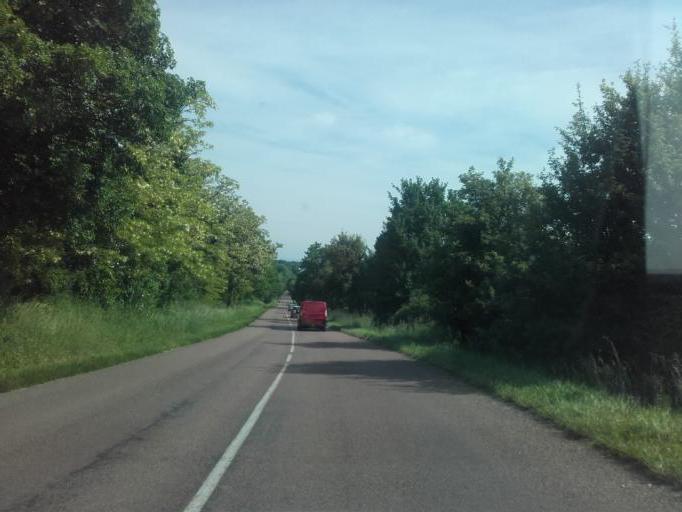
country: FR
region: Bourgogne
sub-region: Departement de Saone-et-Loire
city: Dracy-le-Fort
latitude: 46.7983
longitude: 4.7518
